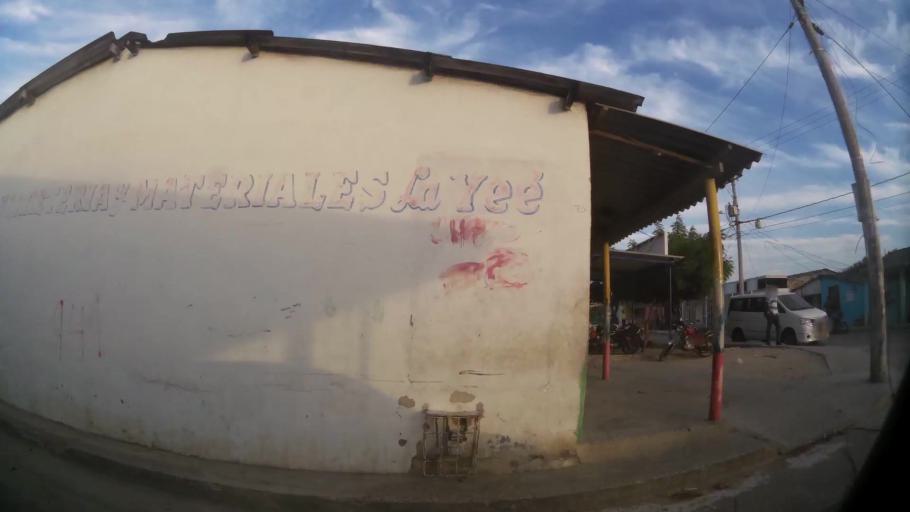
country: CO
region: Atlantico
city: Barranquilla
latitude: 10.9548
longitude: -74.8282
